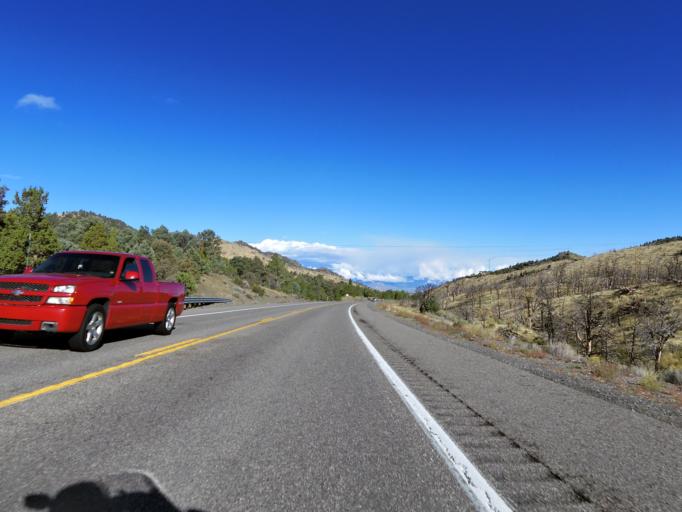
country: US
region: Nevada
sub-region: Douglas County
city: Gardnerville Ranchos
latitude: 38.8221
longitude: -119.6222
